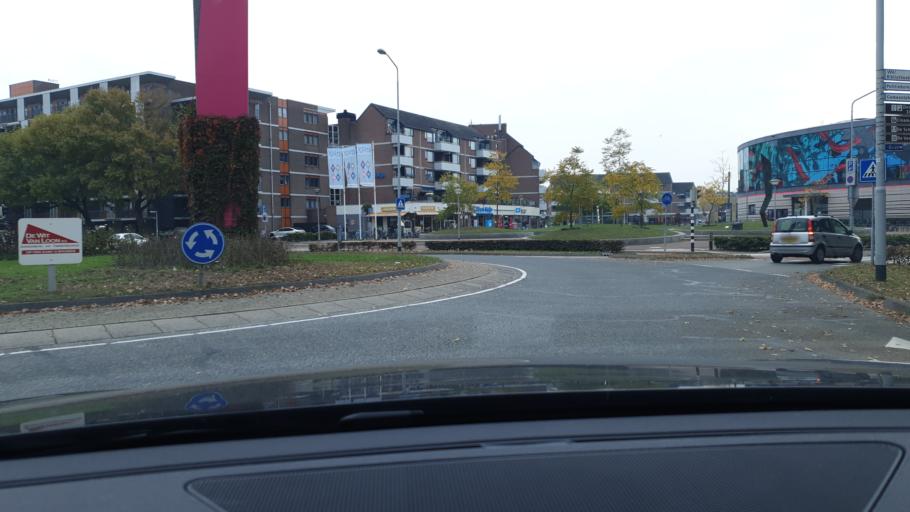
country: NL
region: North Brabant
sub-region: Gemeente Veldhoven
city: Veldhoven
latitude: 51.4224
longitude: 5.4051
